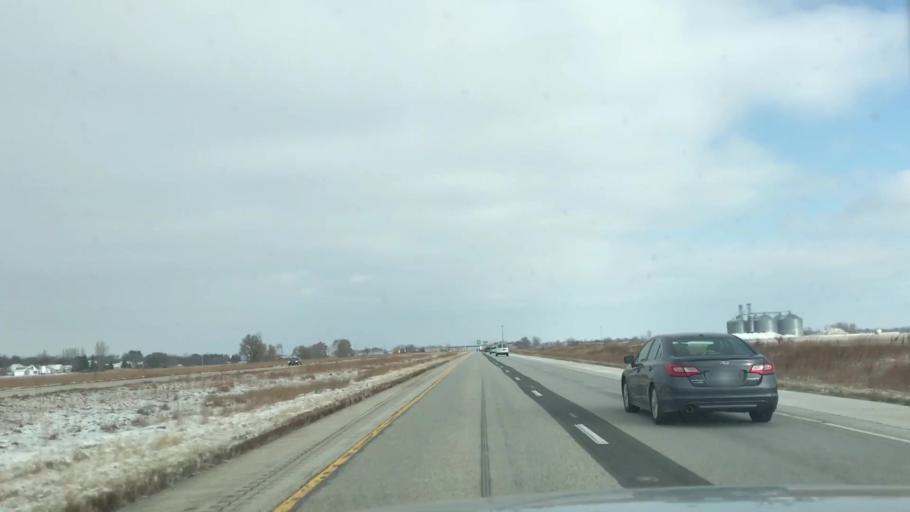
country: US
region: Illinois
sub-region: Sangamon County
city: Divernon
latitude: 39.5556
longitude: -89.6459
